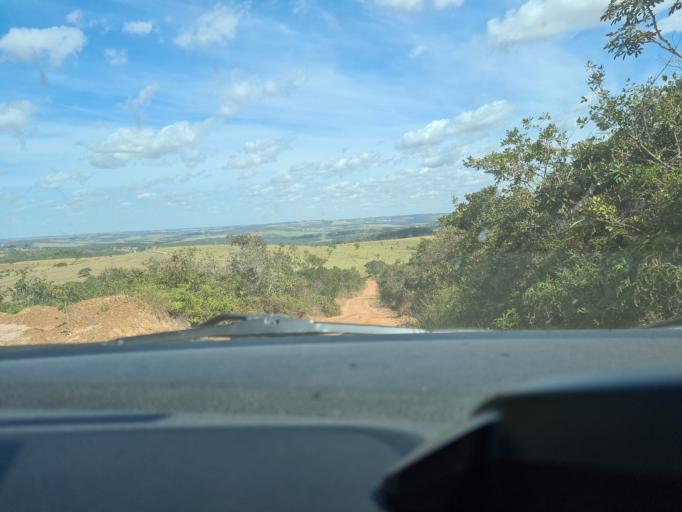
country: BR
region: Goias
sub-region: Silvania
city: Silvania
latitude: -16.5322
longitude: -48.5524
